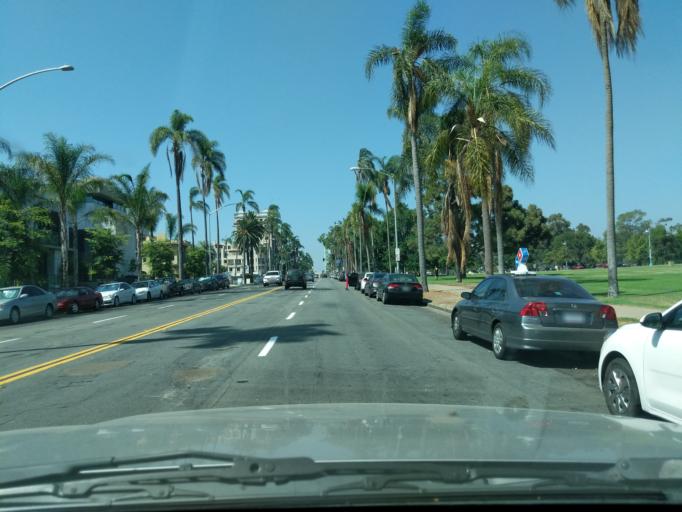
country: US
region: California
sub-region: San Diego County
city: San Diego
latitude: 32.7348
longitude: -117.1594
